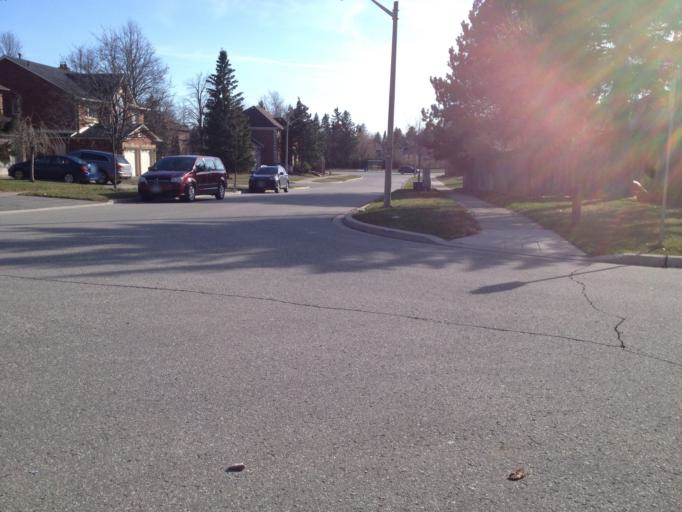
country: CA
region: Ontario
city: Brampton
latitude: 43.7383
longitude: -79.8047
